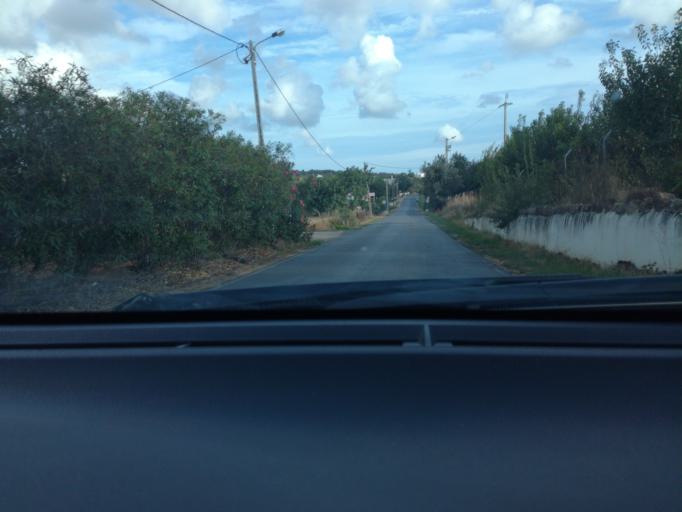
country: PT
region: Faro
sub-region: Sao Bras de Alportel
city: Sao Bras de Alportel
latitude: 37.0879
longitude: -7.8842
